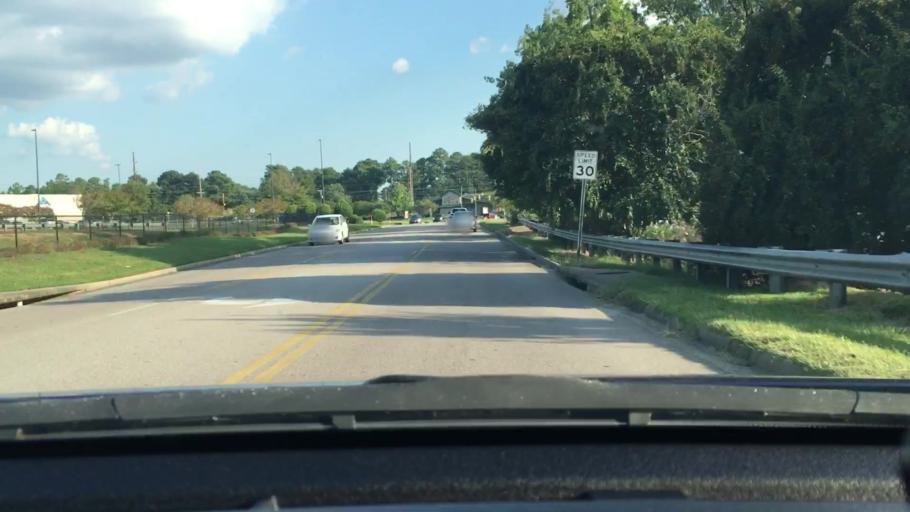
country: US
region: South Carolina
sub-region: Lexington County
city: Seven Oaks
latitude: 34.0727
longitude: -81.1535
